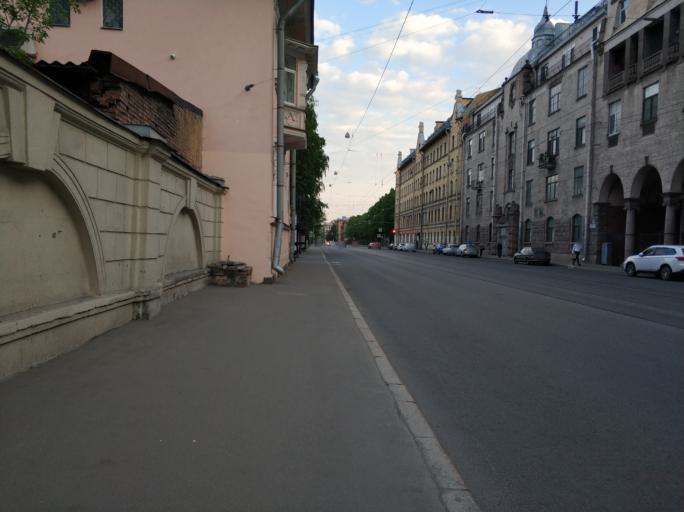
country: RU
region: Leningrad
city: Finlyandskiy
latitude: 59.9668
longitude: 30.3504
